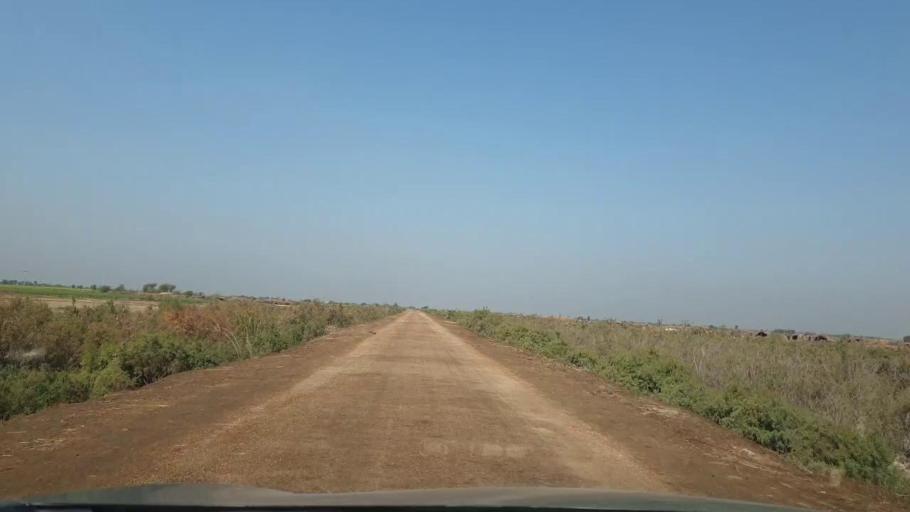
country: PK
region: Sindh
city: Berani
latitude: 25.7018
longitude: 68.8684
